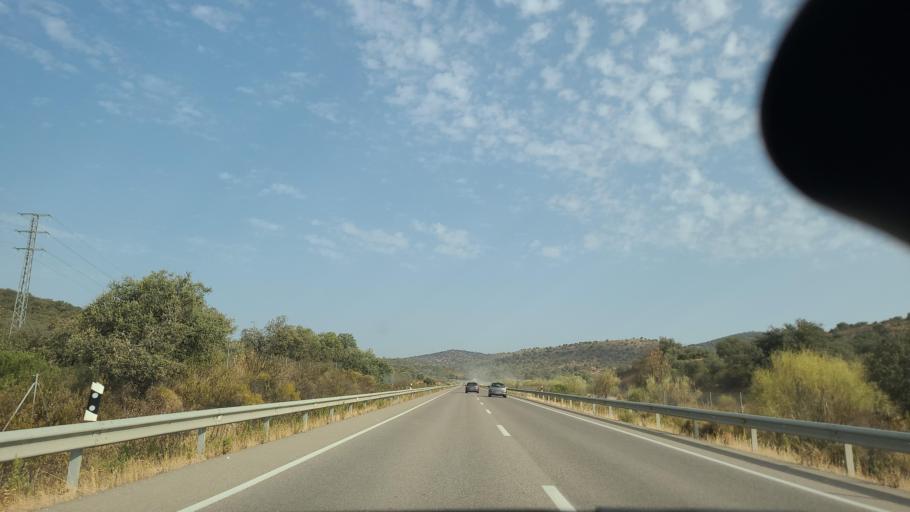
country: ES
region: Andalusia
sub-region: Province of Cordoba
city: Espiel
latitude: 38.1622
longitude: -4.9884
